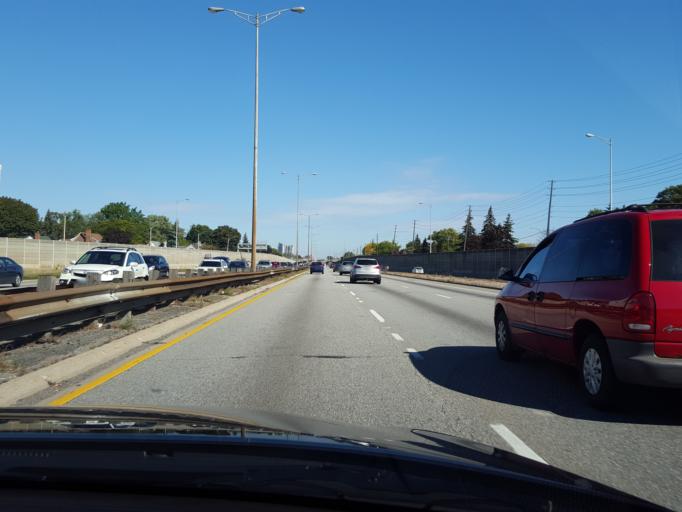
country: CA
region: Ontario
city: Etobicoke
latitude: 43.5843
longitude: -79.5822
